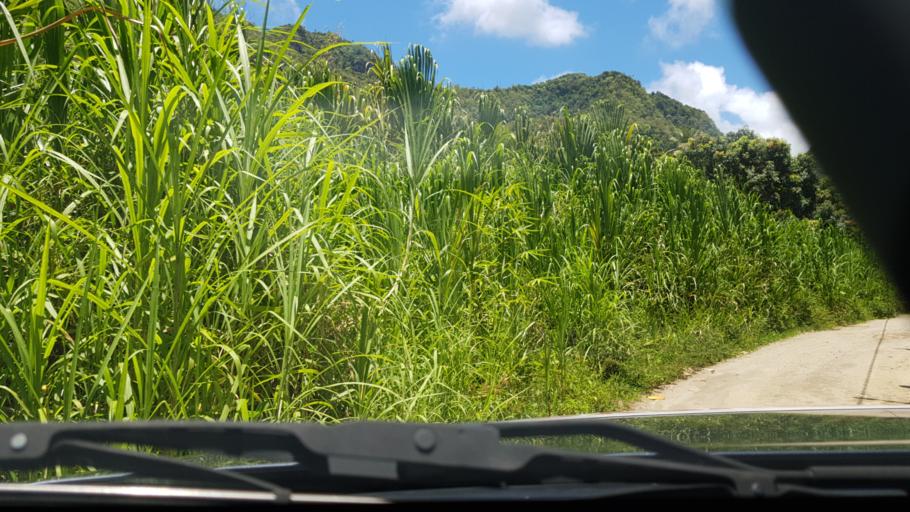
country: LC
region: Anse-la-Raye
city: Canaries
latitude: 13.8983
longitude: -61.0581
